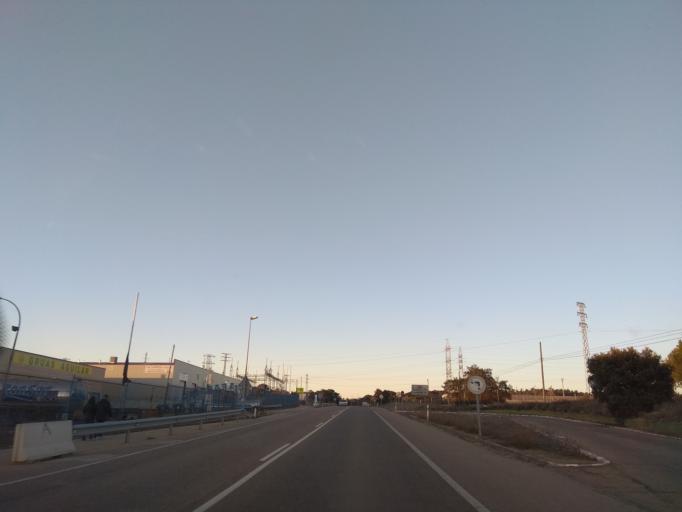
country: ES
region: Castille and Leon
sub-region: Provincia de Burgos
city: Aranda de Duero
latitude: 41.6941
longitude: -3.6842
